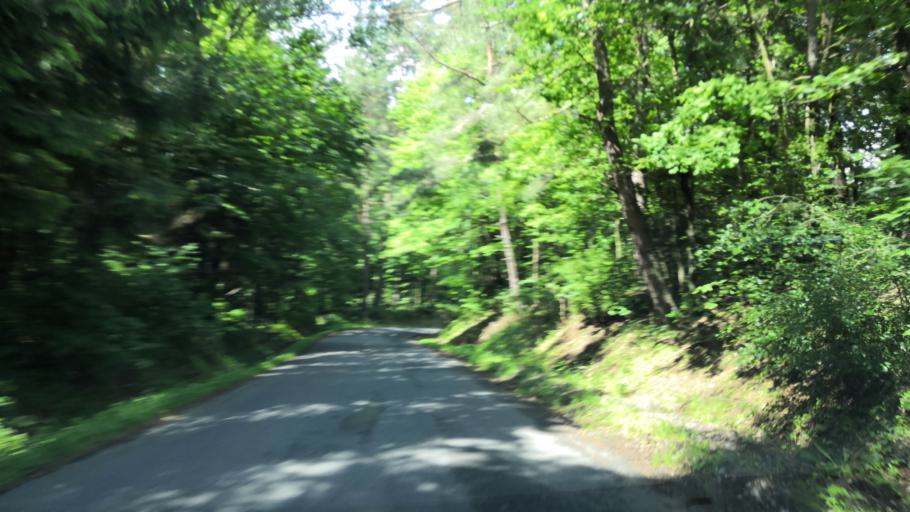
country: CZ
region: Zlin
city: Vidce
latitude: 49.4355
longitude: 18.0939
